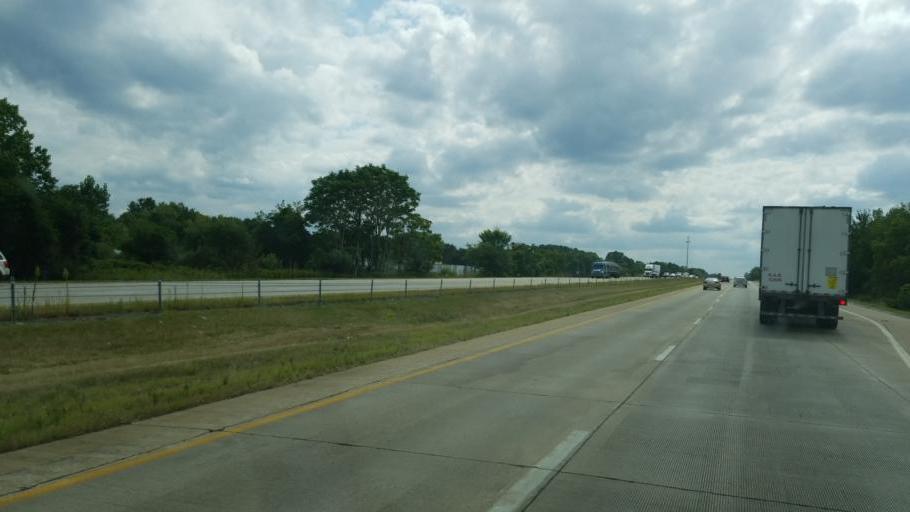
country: US
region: Ohio
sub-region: Portage County
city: Brimfield
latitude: 41.1034
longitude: -81.3739
